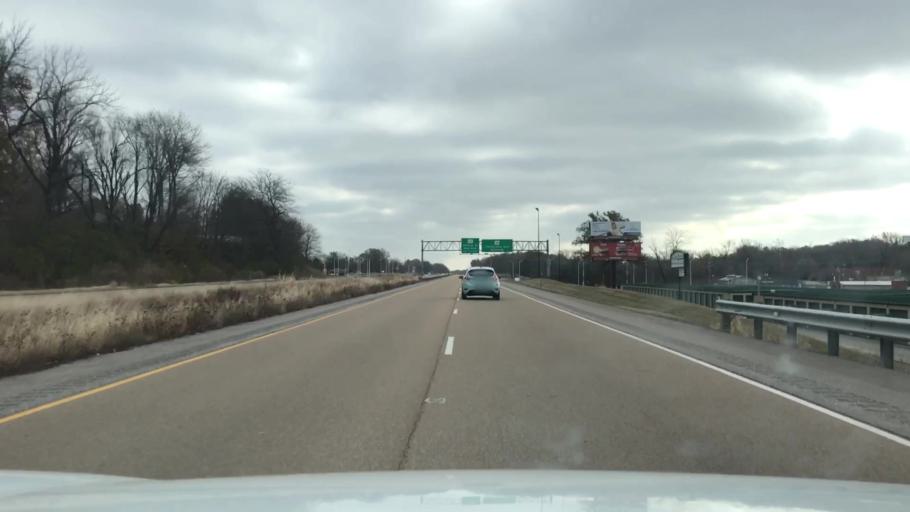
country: US
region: Illinois
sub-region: Saint Clair County
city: Belleville
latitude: 38.5073
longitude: -90.0053
